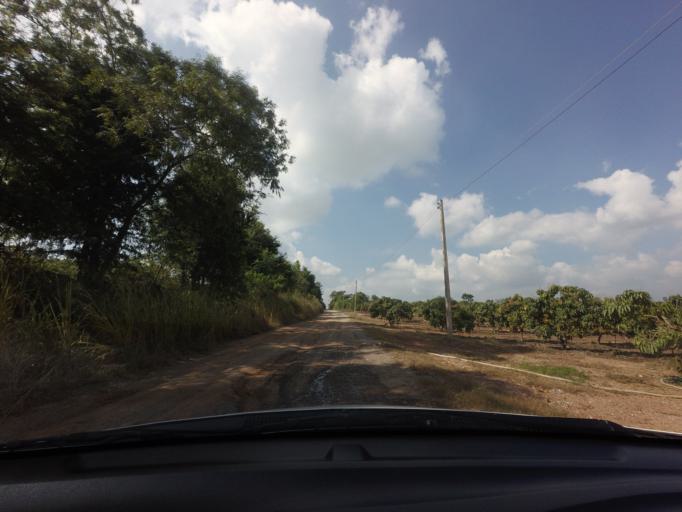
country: TH
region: Nakhon Ratchasima
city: Wang Nam Khiao
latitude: 14.5018
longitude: 101.6298
